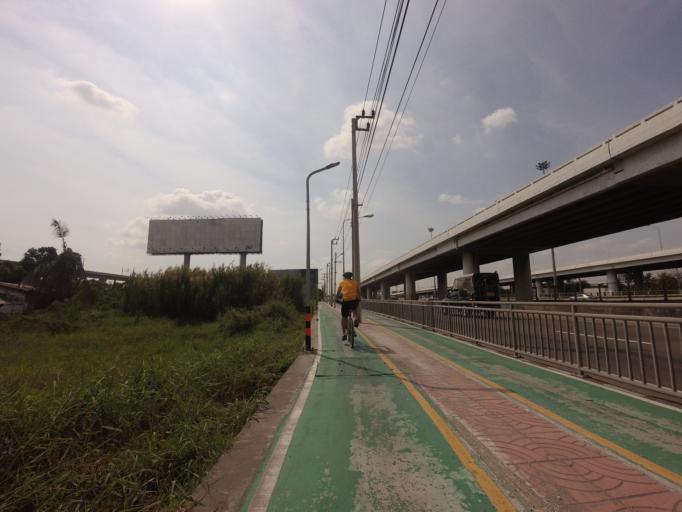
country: TH
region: Bangkok
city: Lat Krabang
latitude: 13.7293
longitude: 100.7570
